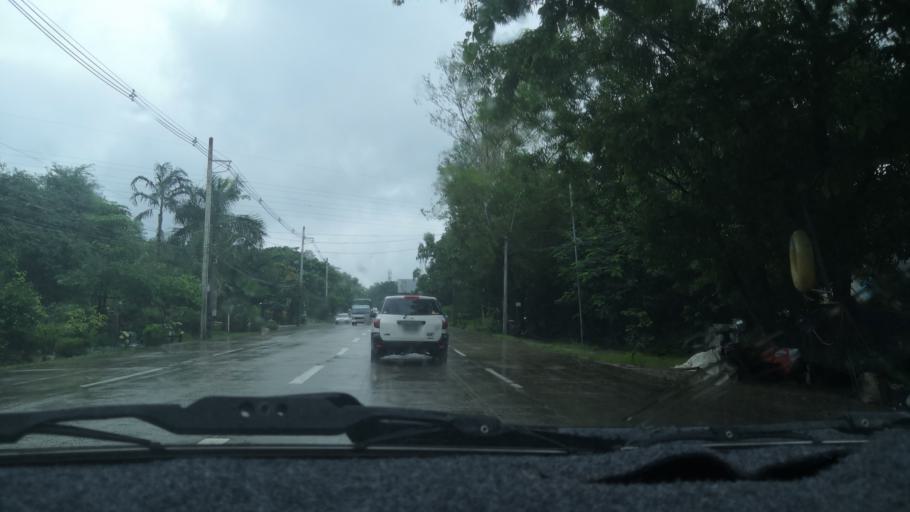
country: MM
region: Yangon
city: Yangon
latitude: 16.8885
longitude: 96.1492
